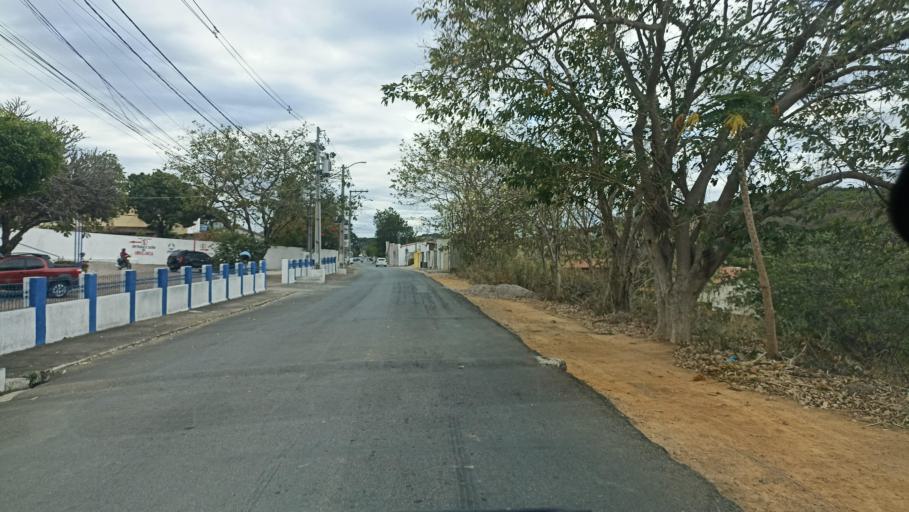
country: BR
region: Bahia
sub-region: Andarai
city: Vera Cruz
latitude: -12.8166
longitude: -41.3317
